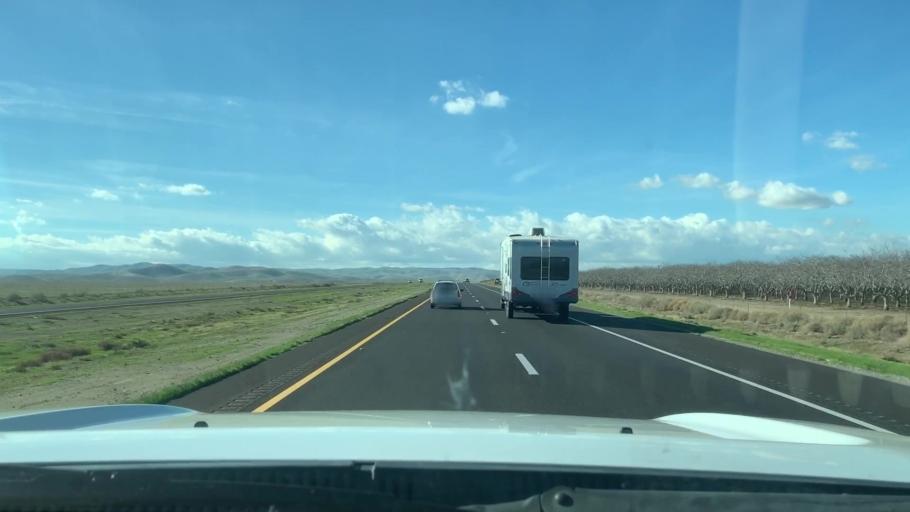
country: US
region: California
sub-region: Kern County
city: Lost Hills
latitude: 35.6146
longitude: -119.9345
